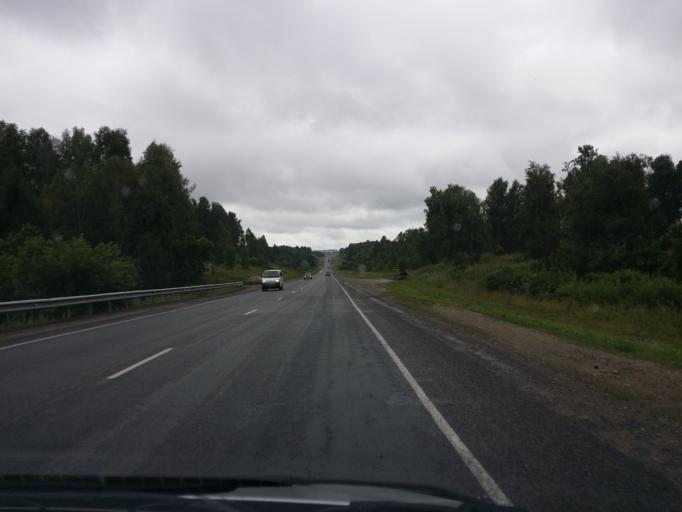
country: RU
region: Altai Krai
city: Troitskoye
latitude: 53.0094
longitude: 84.7231
